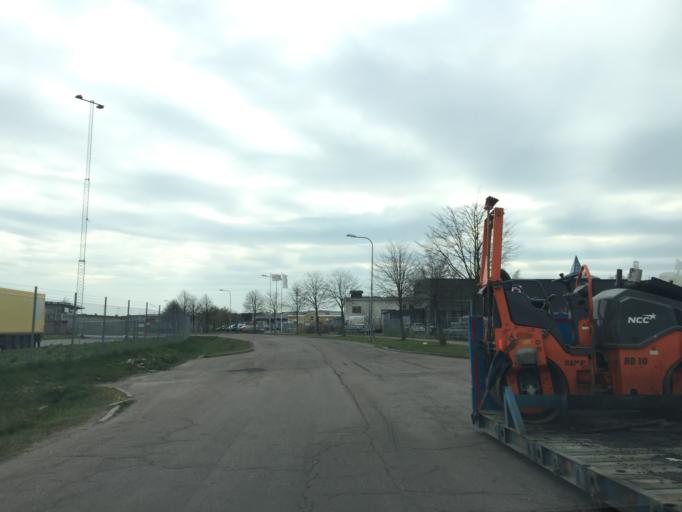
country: SE
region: Vaestra Goetaland
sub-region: Goteborg
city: Gardsten
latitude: 57.7953
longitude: 12.0075
